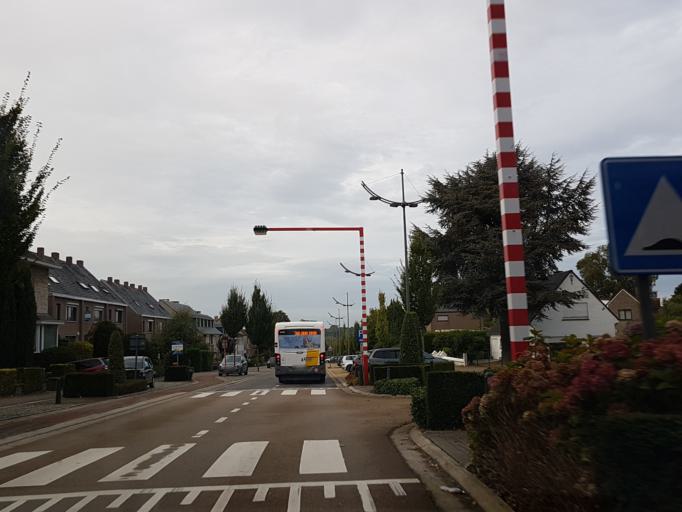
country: BE
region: Flanders
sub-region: Provincie Vlaams-Brabant
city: Kraainem
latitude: 50.8567
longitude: 4.4652
